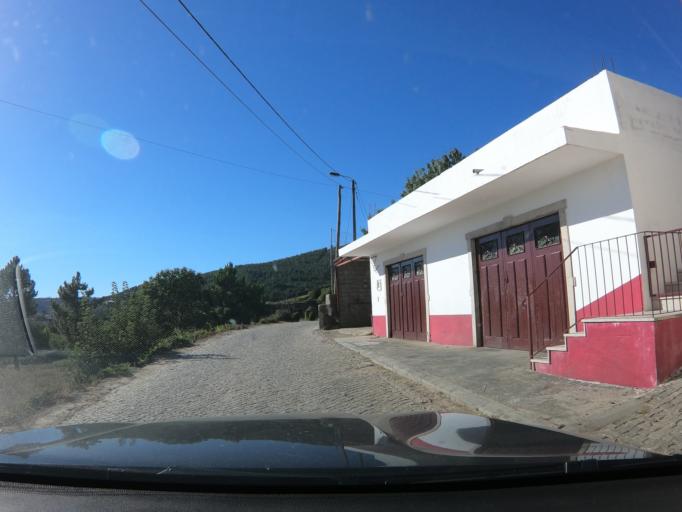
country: PT
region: Vila Real
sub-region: Sabrosa
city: Vilela
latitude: 41.2186
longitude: -7.5650
